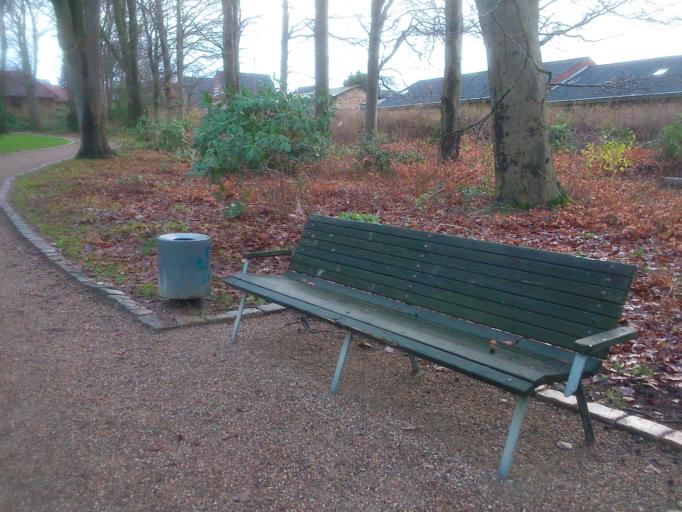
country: DK
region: Central Jutland
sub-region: Ikast-Brande Kommune
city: Ikast
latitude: 56.1418
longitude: 9.1646
